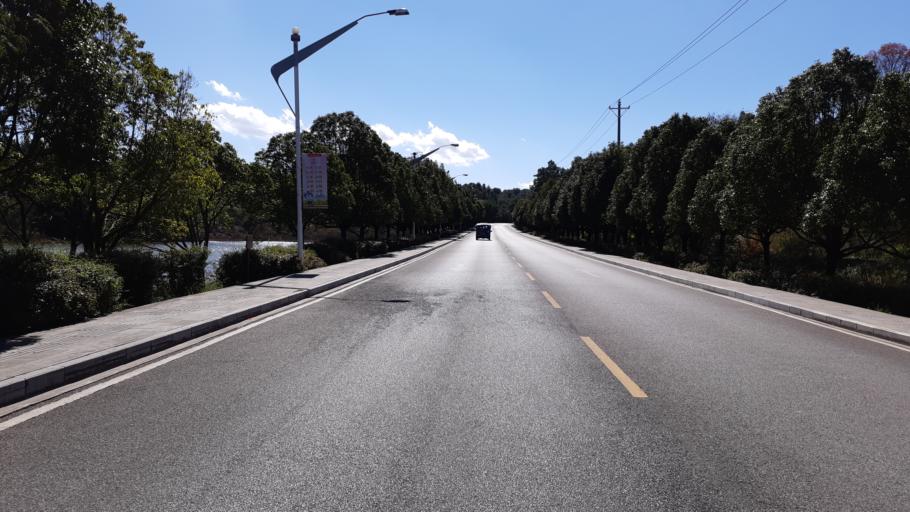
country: CN
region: Yunnan
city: Shilin
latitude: 24.8374
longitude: 103.3267
